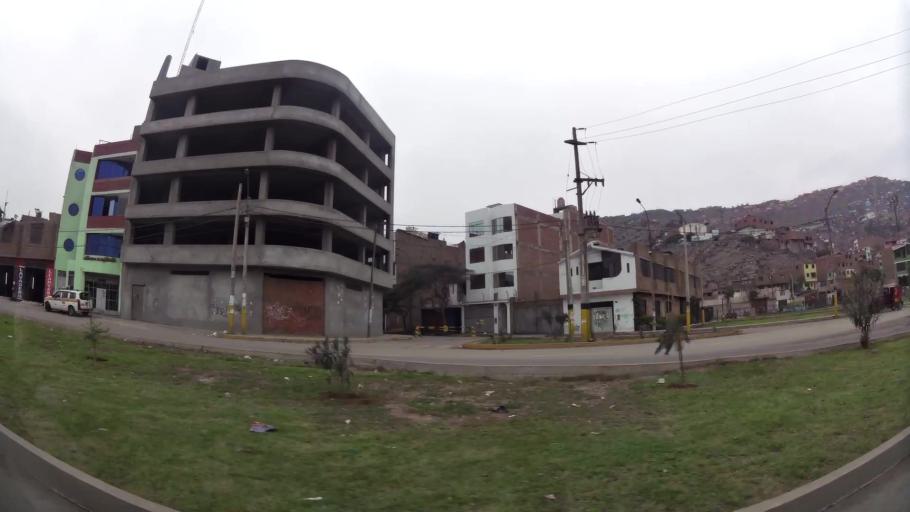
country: PE
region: Lima
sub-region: Lima
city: Vitarte
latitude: -12.0411
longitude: -76.9242
